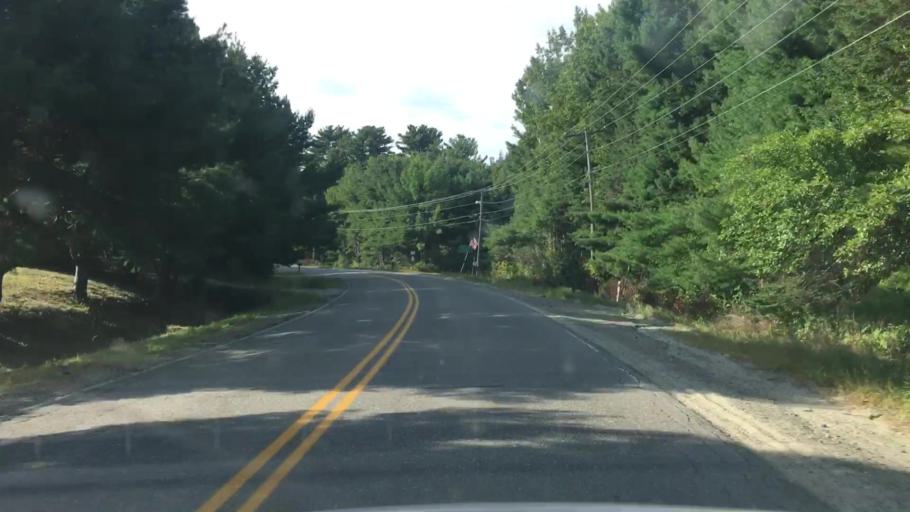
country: US
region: Maine
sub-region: Penobscot County
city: Enfield
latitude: 45.2359
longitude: -68.5446
